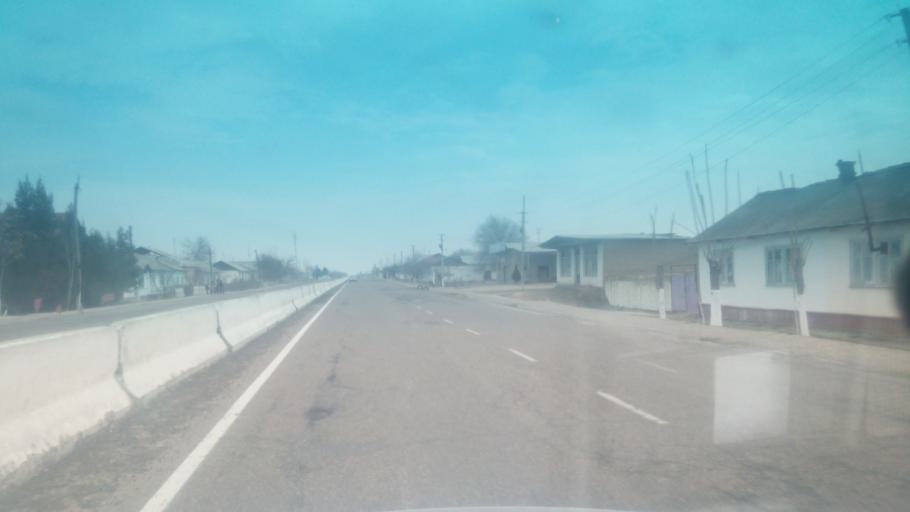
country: KZ
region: Ongtustik Qazaqstan
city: Myrzakent
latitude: 40.4998
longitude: 68.5684
